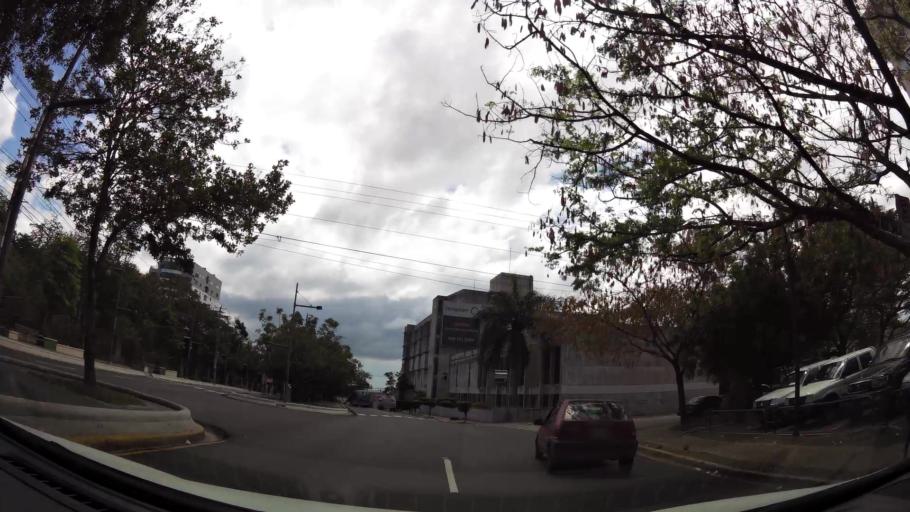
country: DO
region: Nacional
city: La Julia
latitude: 18.4661
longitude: -69.9213
